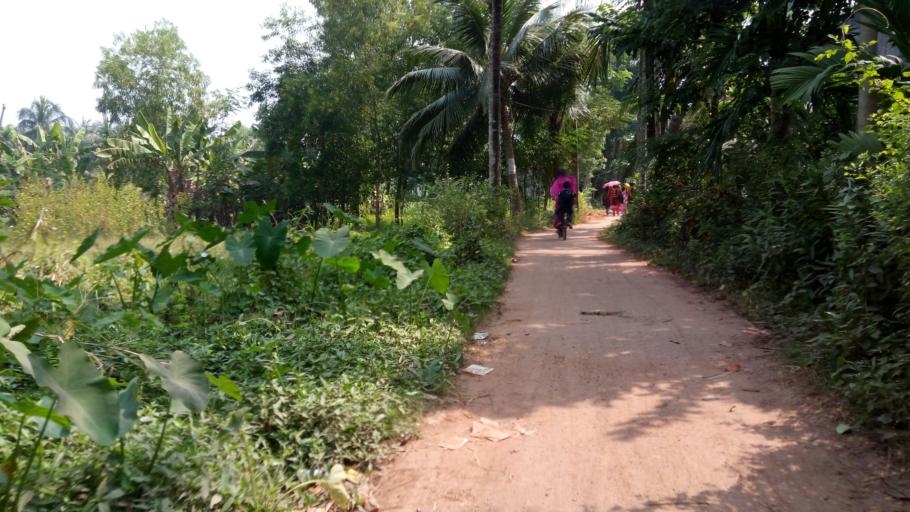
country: IN
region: West Bengal
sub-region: Purba Medinipur
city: Mahishadal
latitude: 22.1737
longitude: 87.9113
